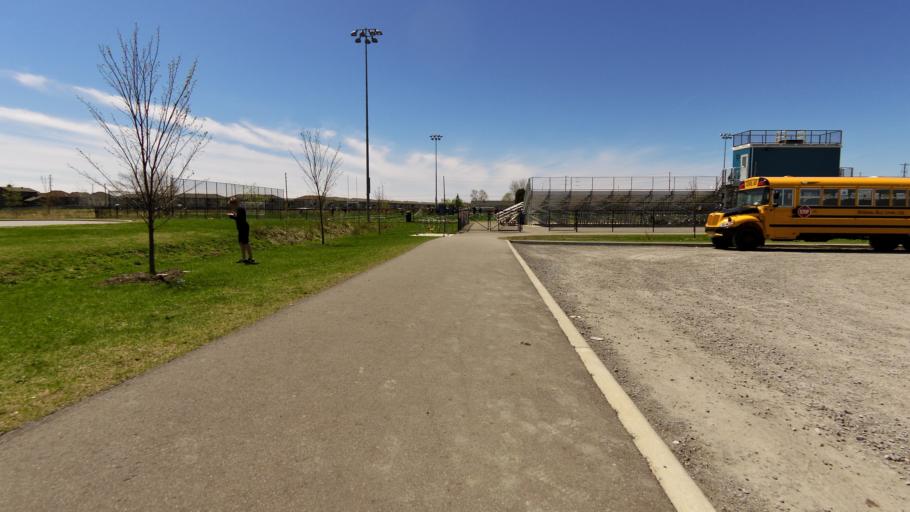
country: CA
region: Ontario
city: Clarence-Rockland
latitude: 45.4650
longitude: -75.4488
